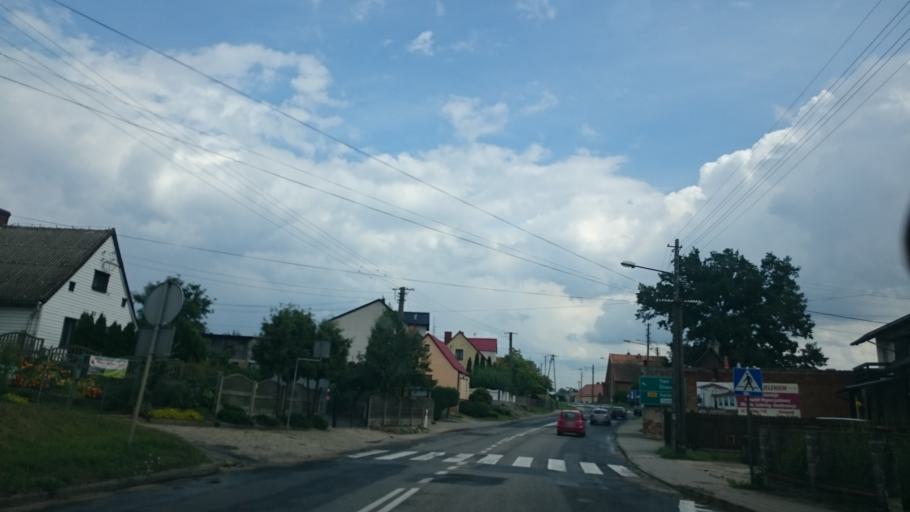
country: PL
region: Kujawsko-Pomorskie
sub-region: Powiat tucholski
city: Tuchola
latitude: 53.5932
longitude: 17.8639
